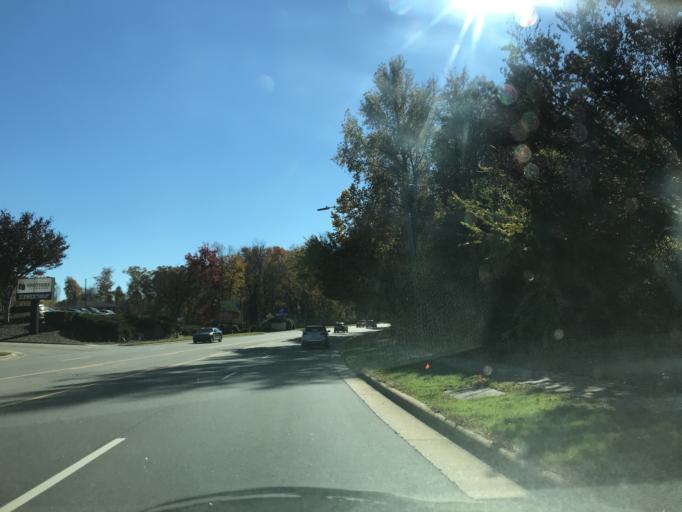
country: US
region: North Carolina
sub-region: Wake County
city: Raleigh
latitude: 35.8536
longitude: -78.5995
